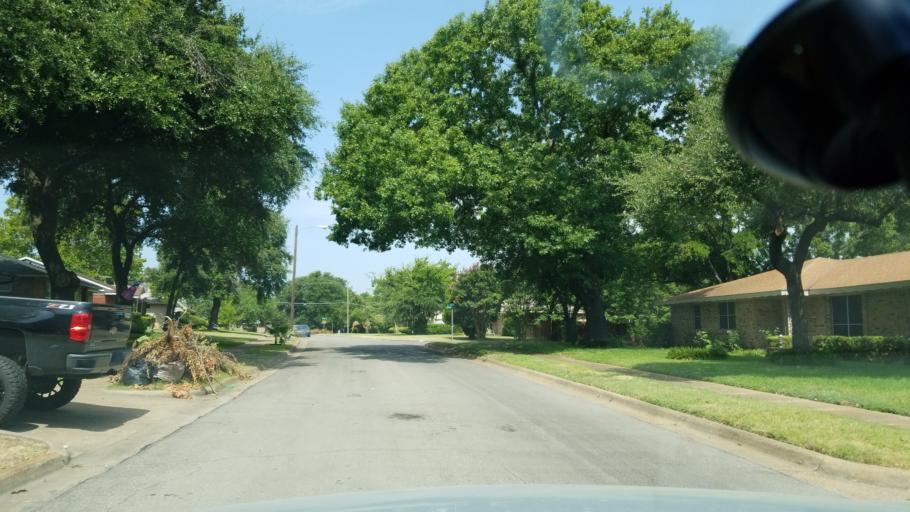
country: US
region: Texas
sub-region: Dallas County
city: Cockrell Hill
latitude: 32.6873
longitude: -96.8422
